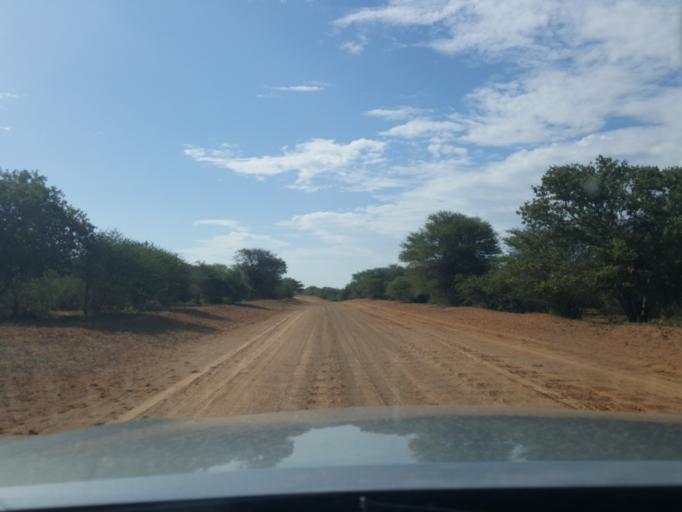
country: BW
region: Kweneng
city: Khudumelapye
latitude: -23.5387
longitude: 24.7283
